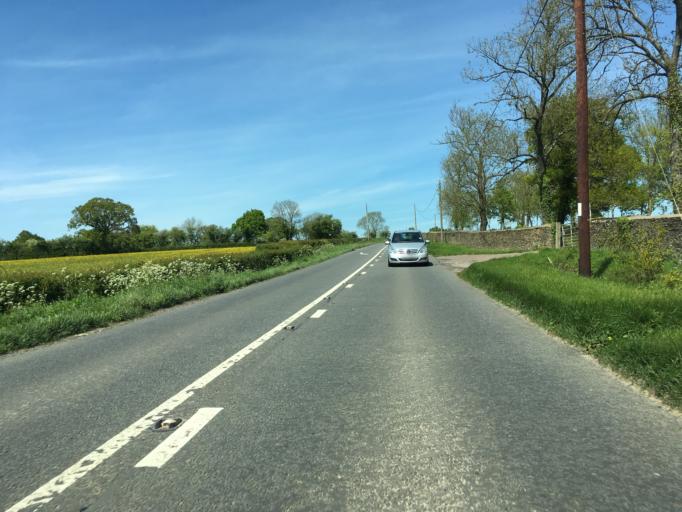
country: GB
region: England
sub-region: Wiltshire
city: Malmesbury
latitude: 51.5987
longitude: -2.0882
